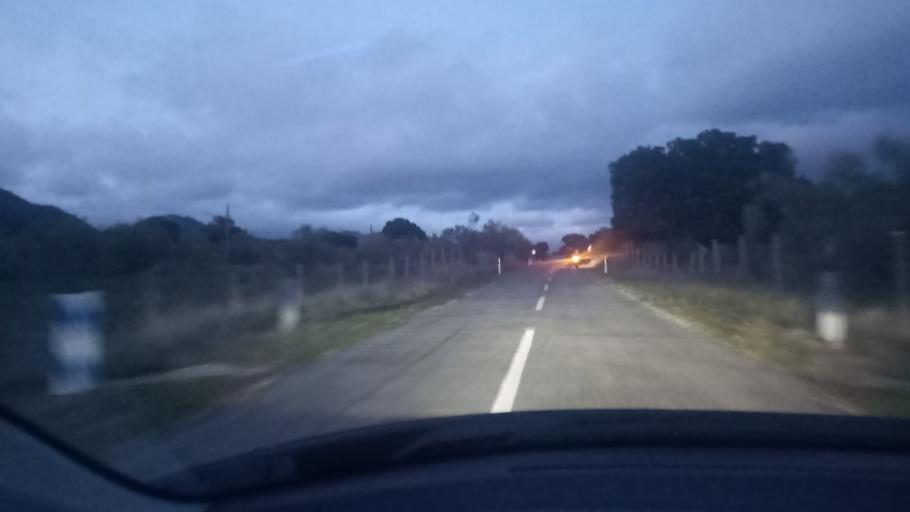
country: ES
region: Madrid
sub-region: Provincia de Madrid
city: Navas del Rey
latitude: 40.4343
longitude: -4.2454
